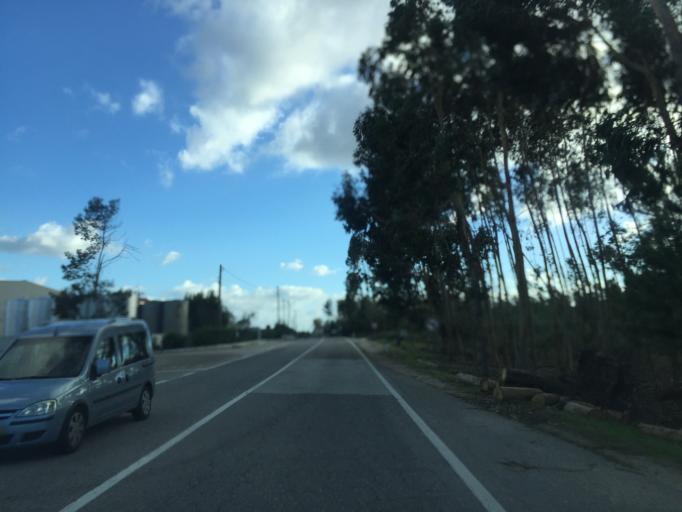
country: PT
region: Leiria
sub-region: Pombal
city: Lourical
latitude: 40.0050
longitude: -8.8059
